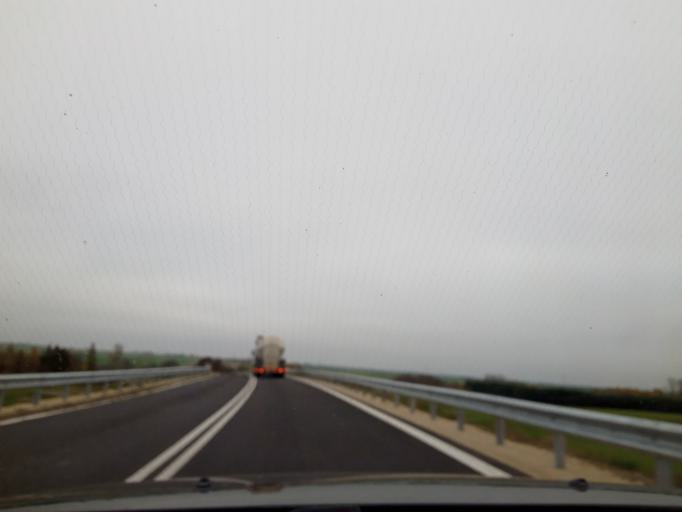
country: PL
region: Swietokrzyskie
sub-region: Powiat jedrzejowski
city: Jedrzejow
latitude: 50.6267
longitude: 20.3259
